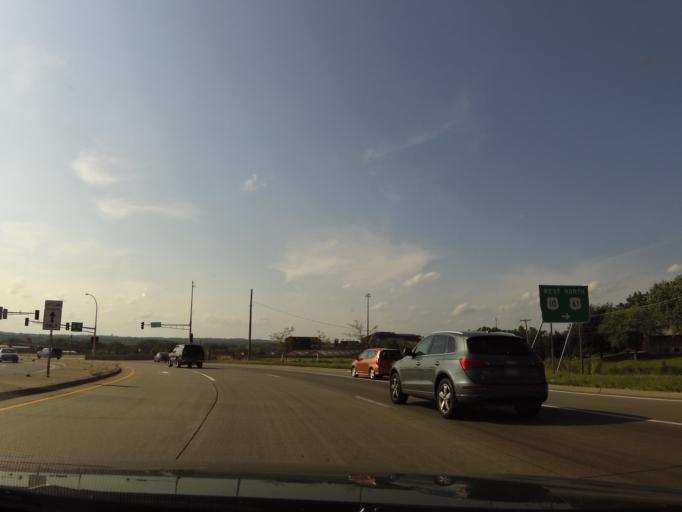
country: US
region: Minnesota
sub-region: Washington County
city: Newport
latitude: 44.8912
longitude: -93.0053
